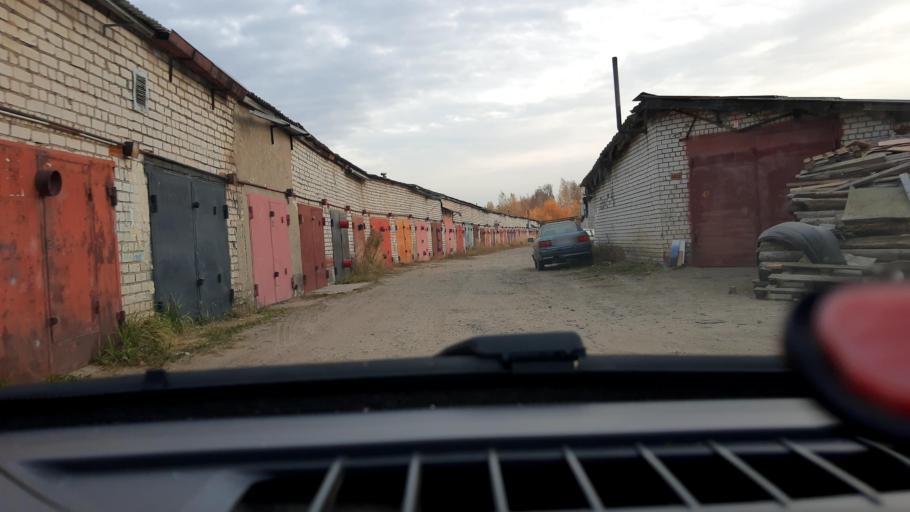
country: RU
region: Nizjnij Novgorod
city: Gorbatovka
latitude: 56.3318
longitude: 43.8162
